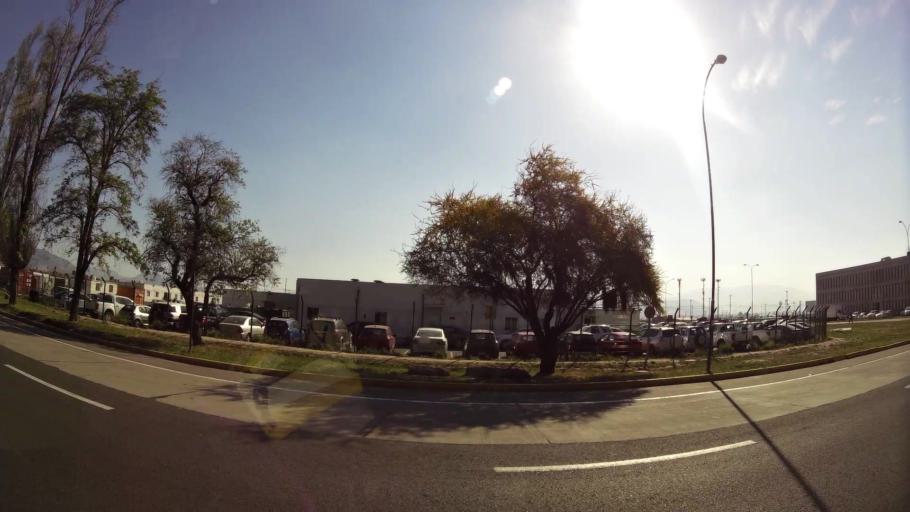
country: CL
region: Santiago Metropolitan
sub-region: Provincia de Santiago
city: Lo Prado
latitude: -33.4082
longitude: -70.7917
